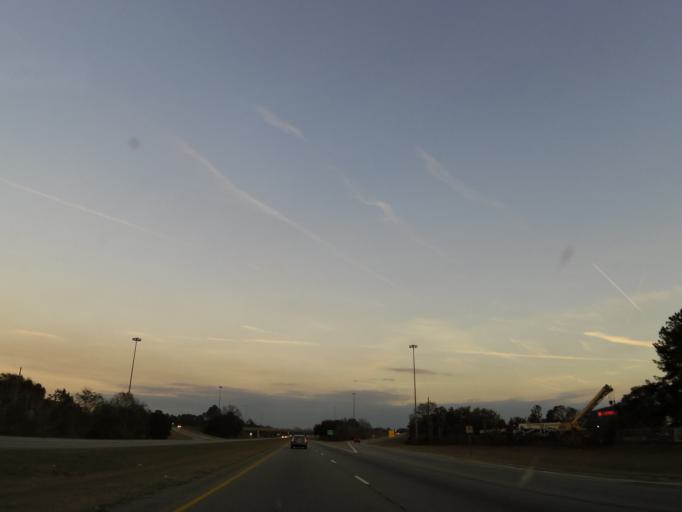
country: US
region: Georgia
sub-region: Dougherty County
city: Albany
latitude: 31.5931
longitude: -84.1294
